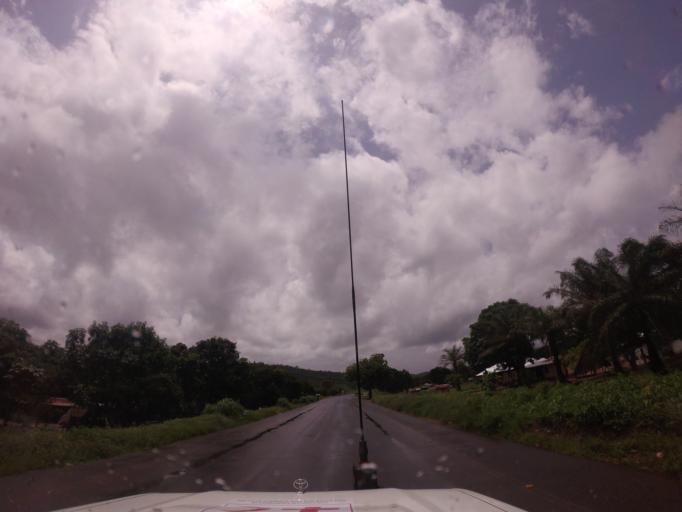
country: SL
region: Northern Province
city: Pepel
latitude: 8.4540
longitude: -12.8537
